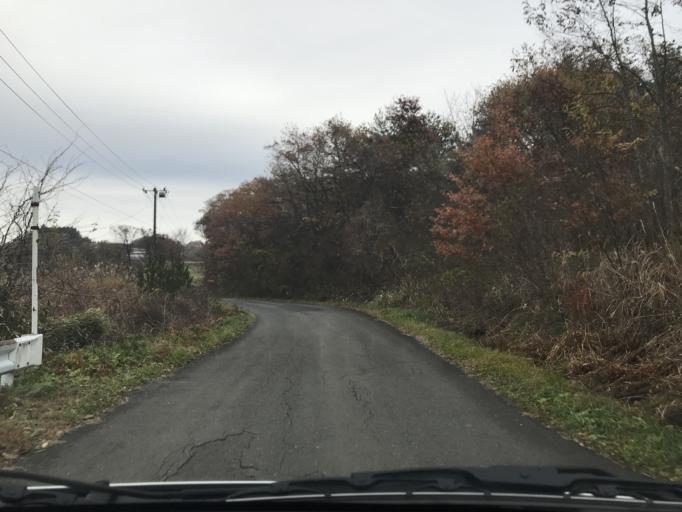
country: JP
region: Iwate
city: Ichinoseki
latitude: 38.9908
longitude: 141.0142
